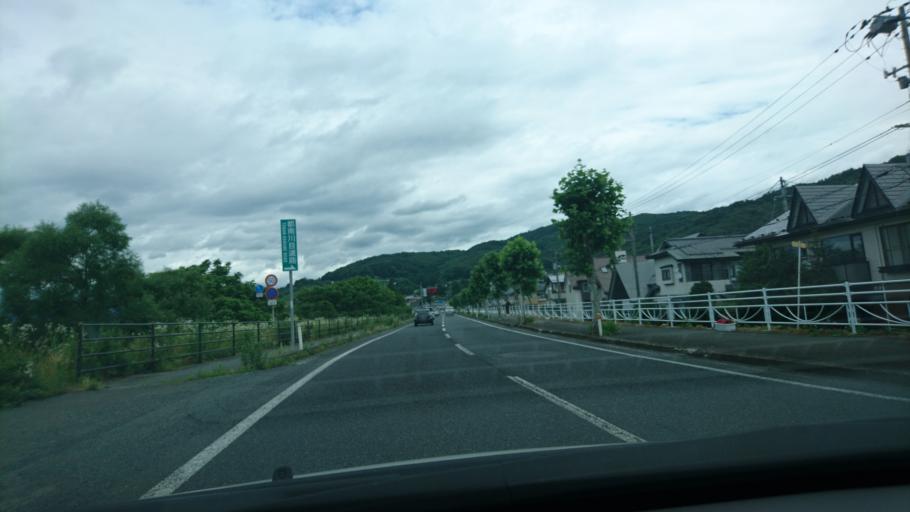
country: JP
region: Iwate
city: Morioka-shi
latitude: 39.6528
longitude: 141.1825
